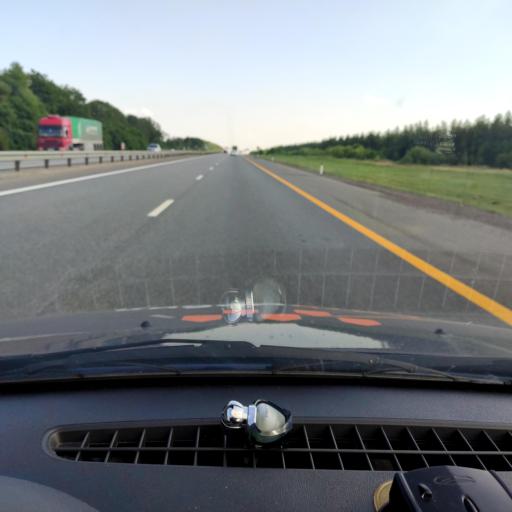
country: RU
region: Lipetsk
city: Zadonsk
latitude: 52.4737
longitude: 38.7657
